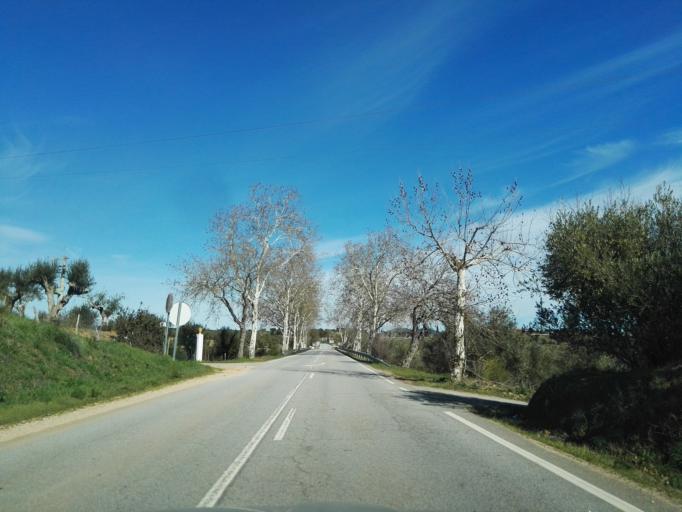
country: PT
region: Portalegre
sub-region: Arronches
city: Arronches
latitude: 39.1293
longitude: -7.2942
